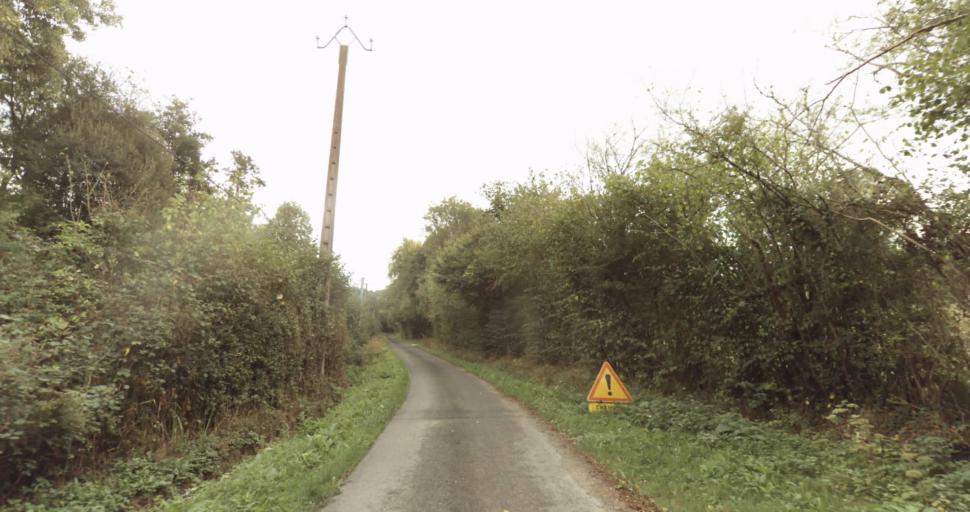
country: FR
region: Lower Normandy
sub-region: Departement de l'Orne
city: Gace
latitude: 48.8268
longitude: 0.2544
